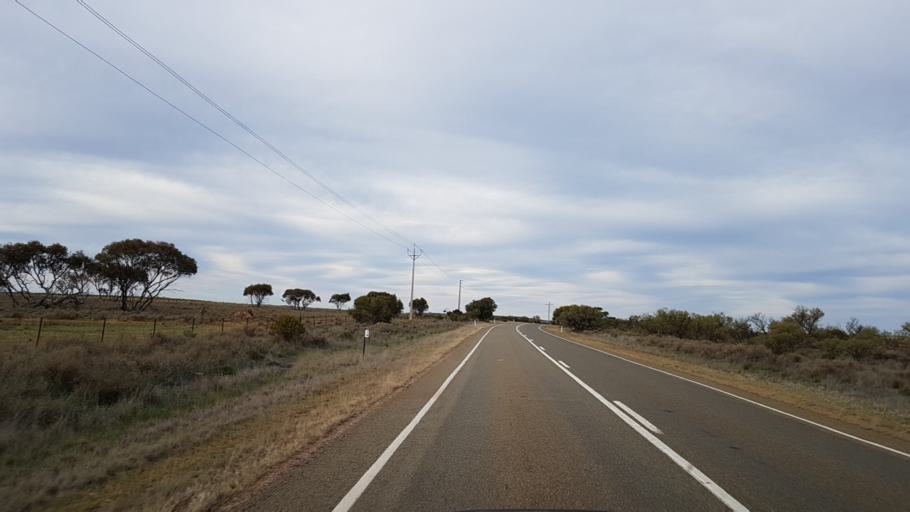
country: AU
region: South Australia
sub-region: Peterborough
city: Peterborough
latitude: -32.9925
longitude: 138.7881
